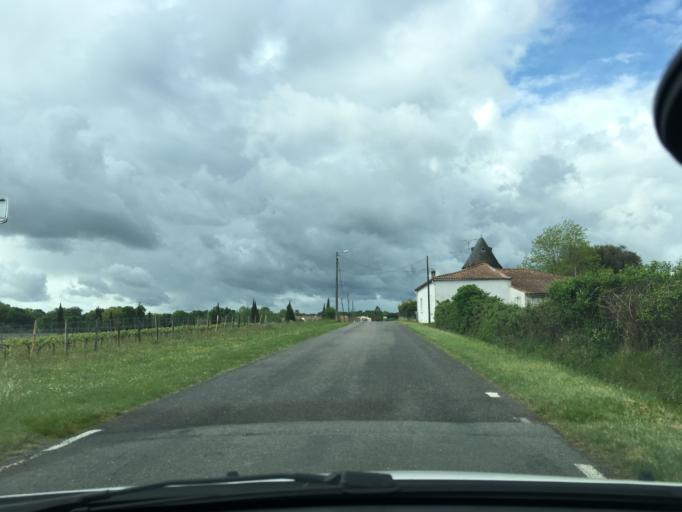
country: FR
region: Aquitaine
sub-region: Departement de la Gironde
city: Vertheuil
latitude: 45.3193
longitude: -0.8365
